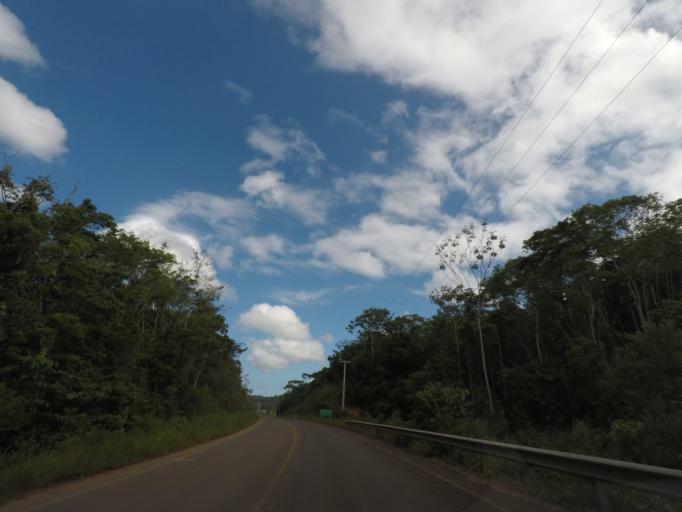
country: BR
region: Bahia
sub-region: Itacare
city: Itacare
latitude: -14.2258
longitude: -39.0966
